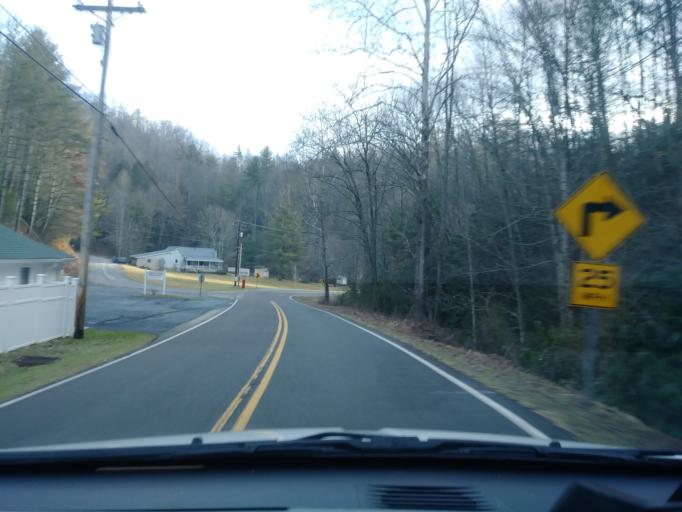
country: US
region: Tennessee
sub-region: Carter County
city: Pine Crest
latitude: 36.2153
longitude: -82.2171
